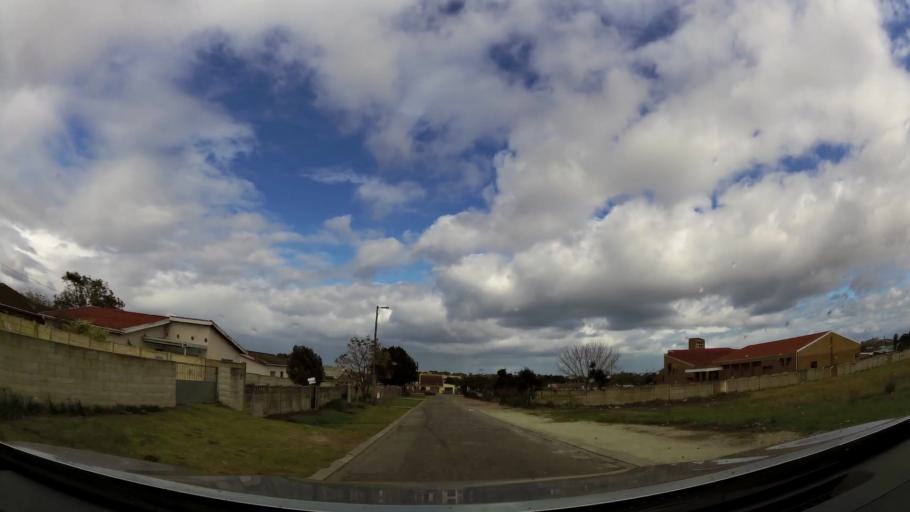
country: ZA
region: Western Cape
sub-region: Eden District Municipality
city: George
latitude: -34.0212
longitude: 22.4671
